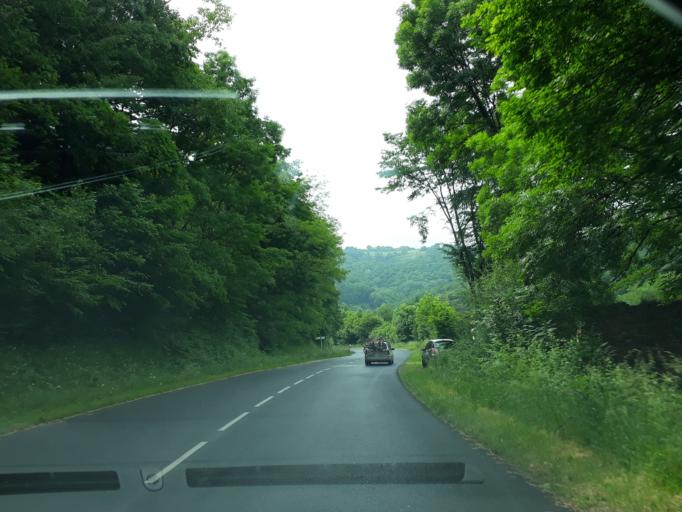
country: FR
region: Limousin
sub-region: Departement de la Correze
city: Beynat
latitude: 45.1292
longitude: 1.6829
